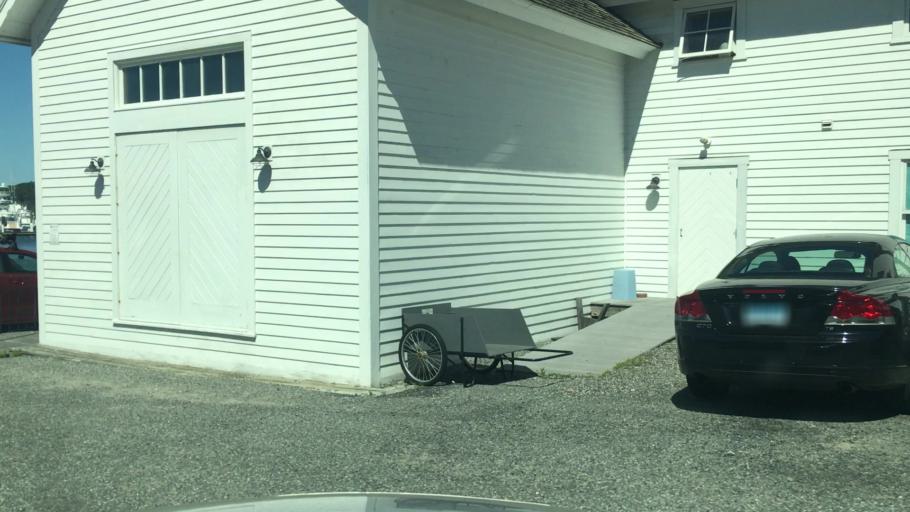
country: US
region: Connecticut
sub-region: Middlesex County
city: Essex Village
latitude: 41.3514
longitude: -72.3849
